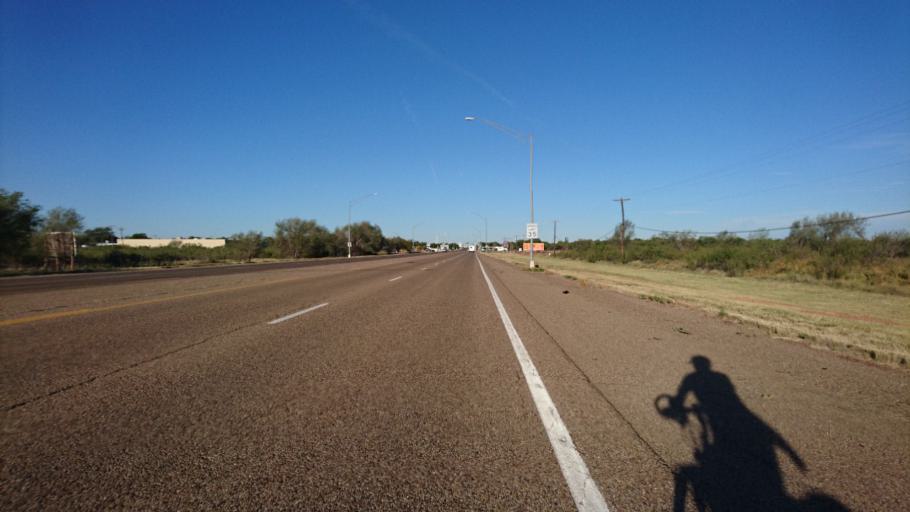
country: US
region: New Mexico
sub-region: Quay County
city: Tucumcari
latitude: 35.1719
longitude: -103.6976
